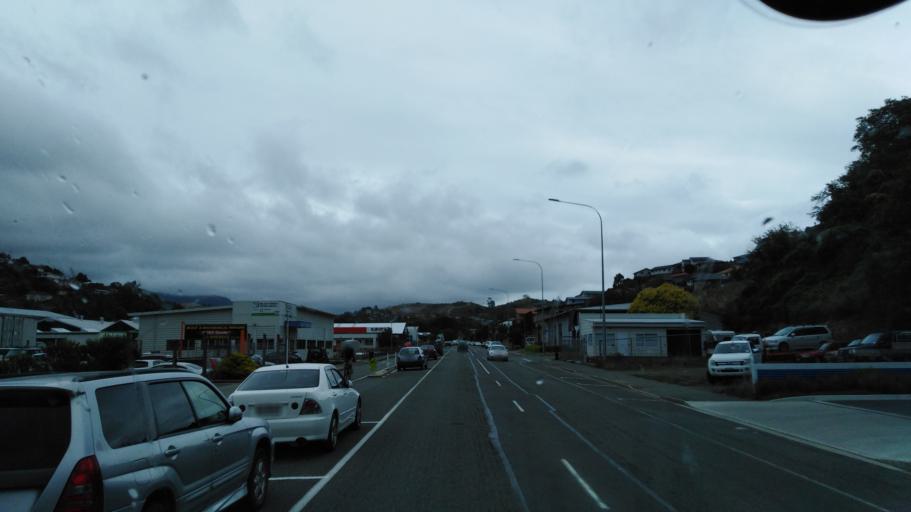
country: NZ
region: Nelson
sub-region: Nelson City
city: Nelson
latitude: -41.2757
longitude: 173.2743
